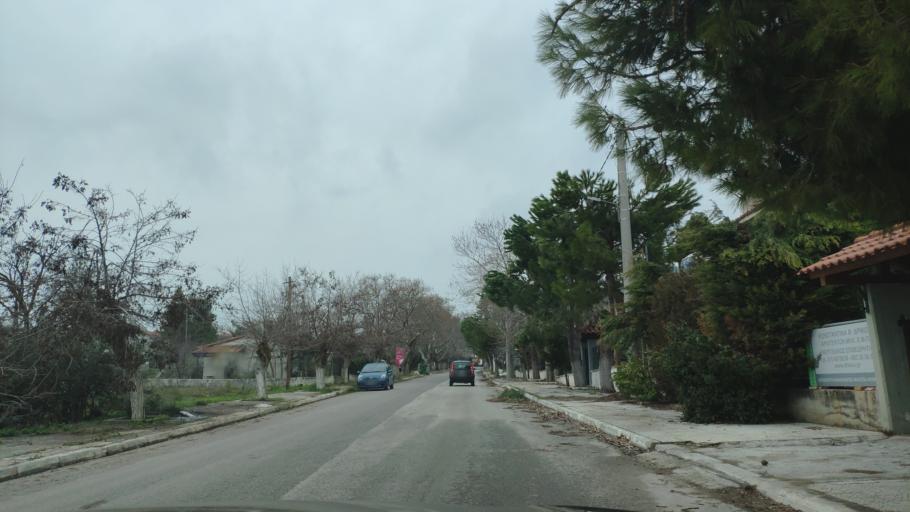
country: GR
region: Attica
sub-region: Nomarchia Dytikis Attikis
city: Vilia
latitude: 38.1690
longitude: 23.3434
